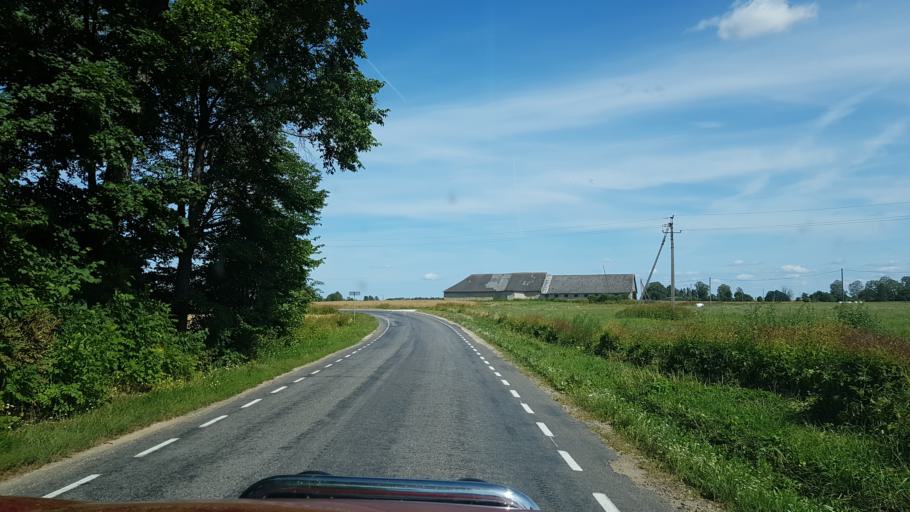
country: EE
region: Jaervamaa
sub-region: Jaerva-Jaani vald
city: Jarva-Jaani
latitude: 59.0385
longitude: 25.9610
